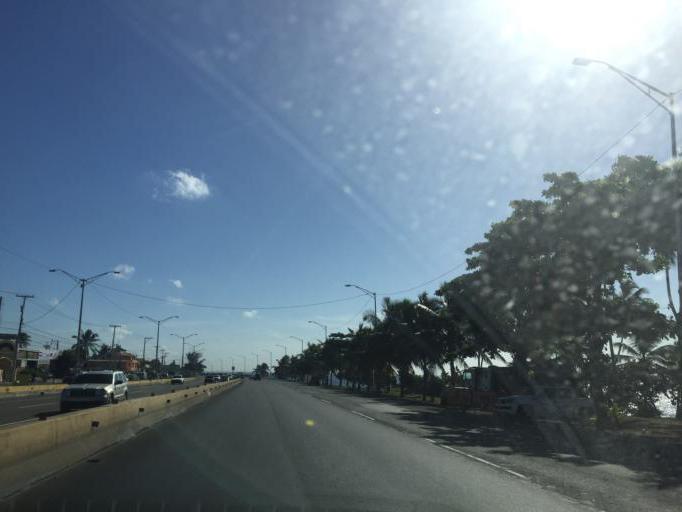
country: DO
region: Santo Domingo
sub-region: Santo Domingo
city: Santo Domingo Este
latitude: 18.4659
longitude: -69.8220
